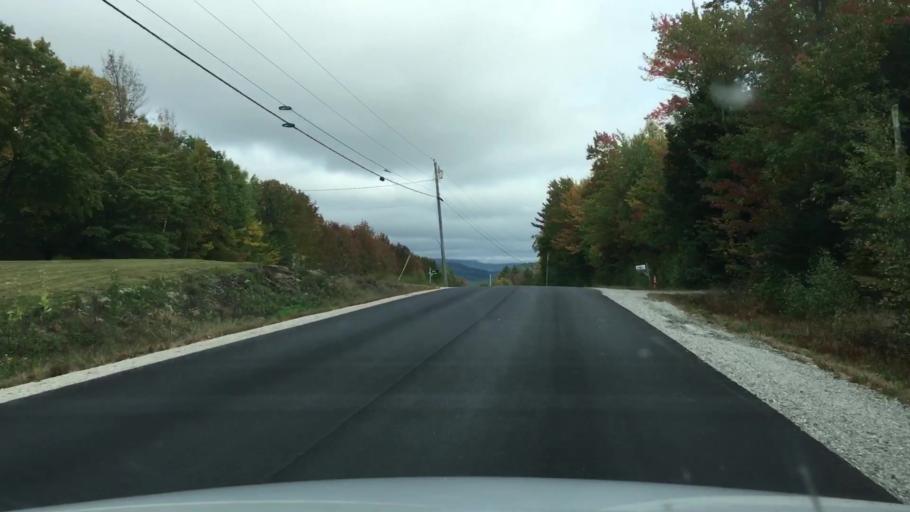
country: US
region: Maine
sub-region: Oxford County
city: Bethel
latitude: 44.3043
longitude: -70.7511
